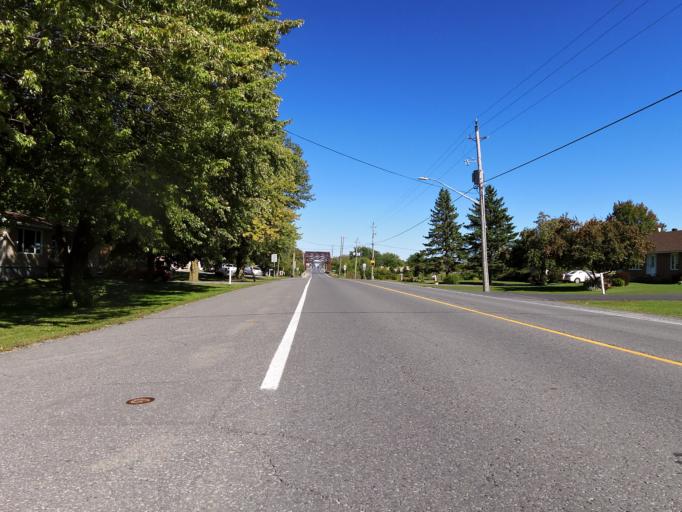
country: CA
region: Ontario
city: Casselman
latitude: 45.2530
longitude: -75.1290
